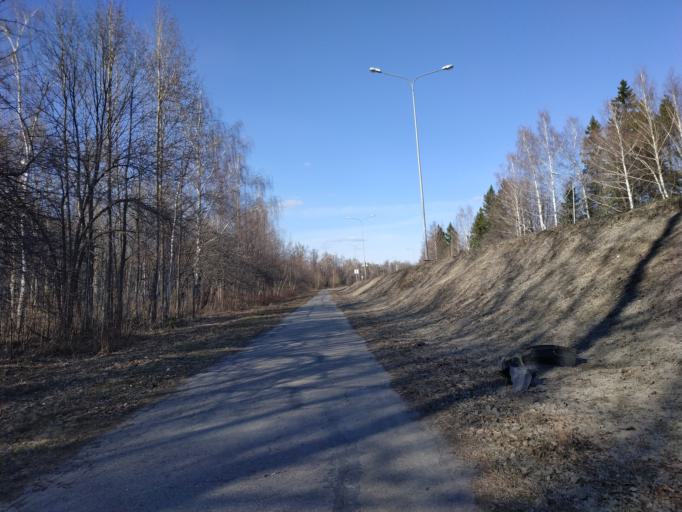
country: RU
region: Chuvashia
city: Ishley
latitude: 56.1220
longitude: 47.0601
